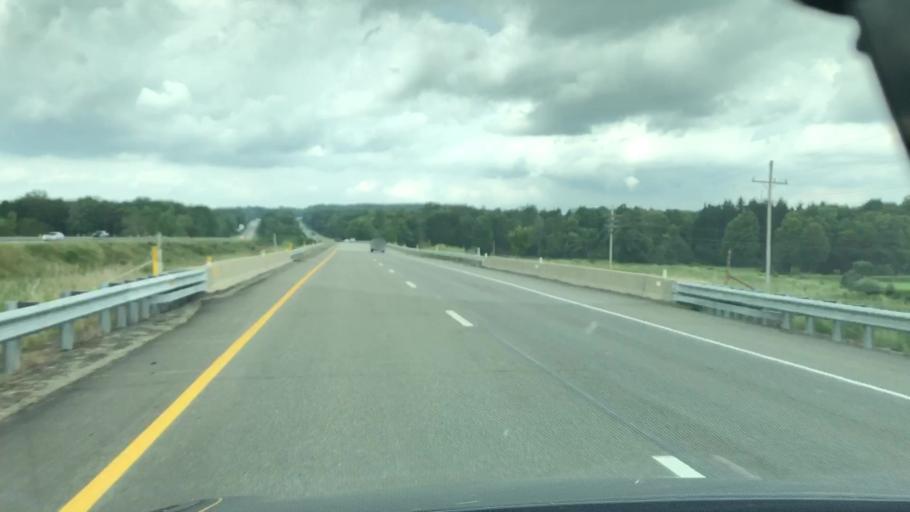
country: US
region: Pennsylvania
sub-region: Erie County
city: Edinboro
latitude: 41.9023
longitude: -80.1754
